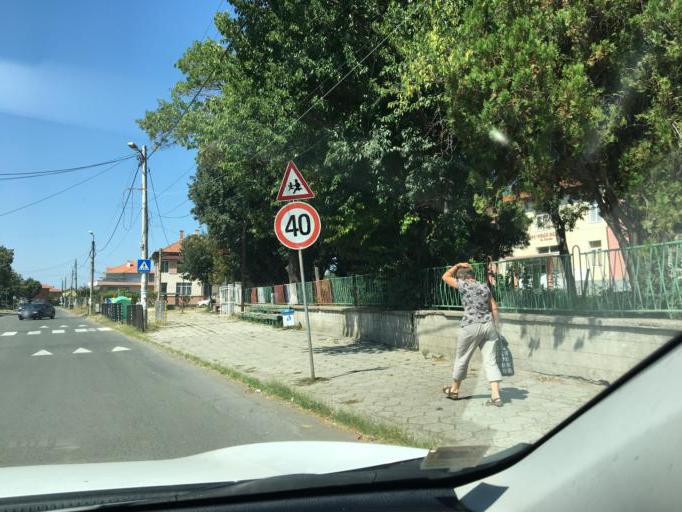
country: BG
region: Burgas
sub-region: Obshtina Kameno
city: Kameno
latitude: 42.6277
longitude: 27.3933
